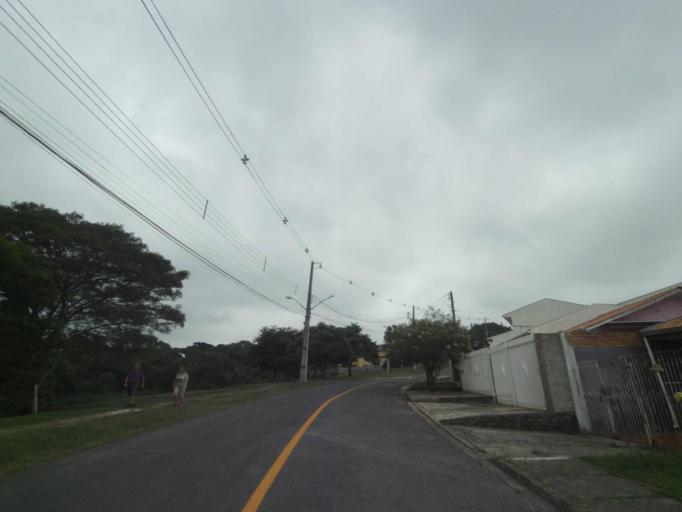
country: BR
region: Parana
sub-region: Curitiba
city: Curitiba
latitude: -25.4882
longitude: -49.3516
